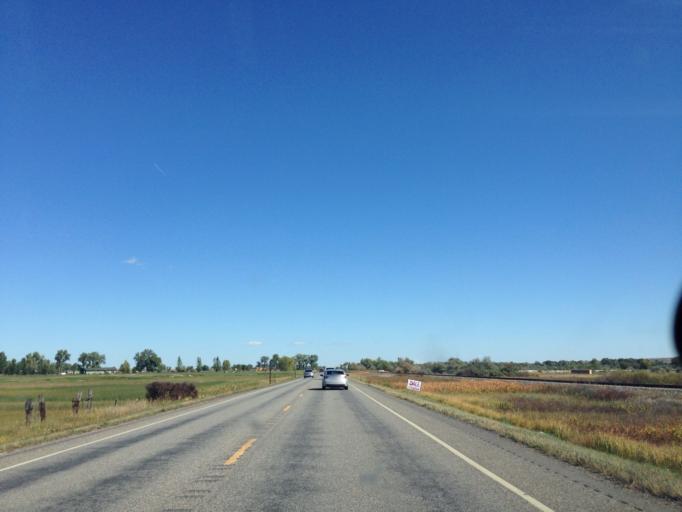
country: US
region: Montana
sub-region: Yellowstone County
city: Laurel
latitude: 45.5960
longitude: -108.8112
